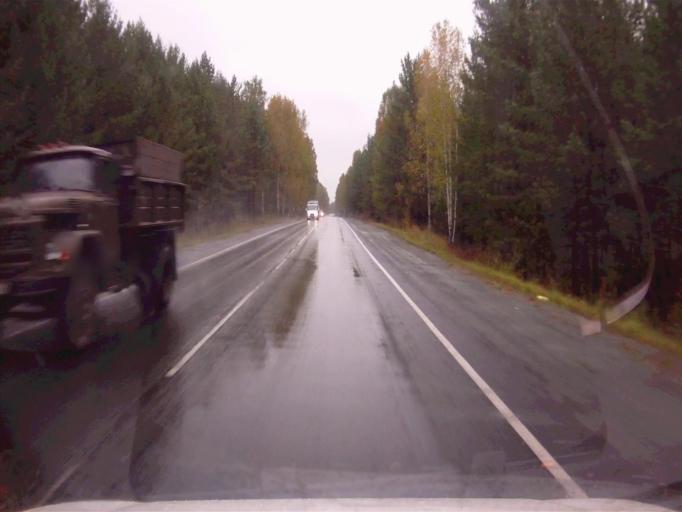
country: RU
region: Chelyabinsk
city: Tayginka
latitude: 55.5828
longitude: 60.6382
